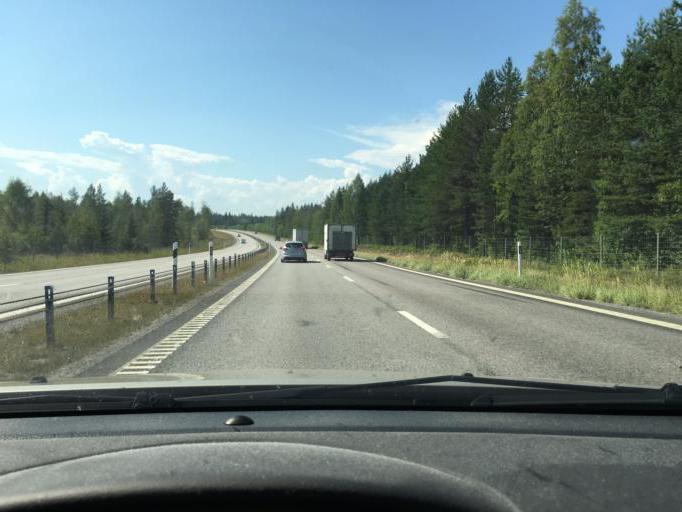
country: SE
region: Norrbotten
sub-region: Lulea Kommun
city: Gammelstad
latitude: 65.5825
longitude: 21.9702
